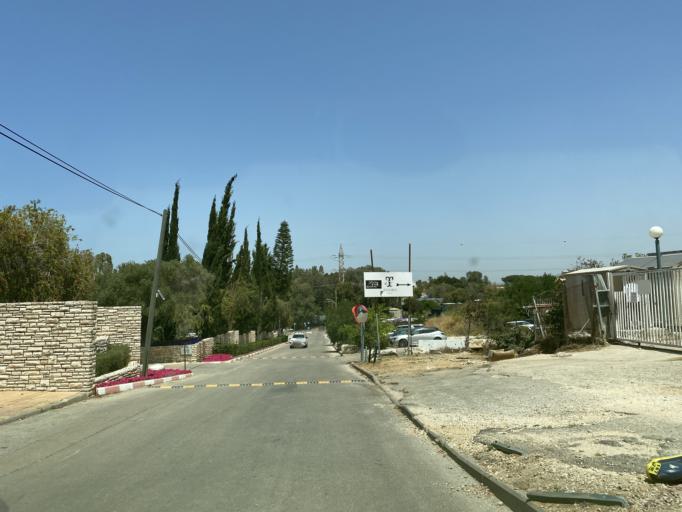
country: IL
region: Tel Aviv
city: Ramat HaSharon
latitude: 32.1301
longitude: 34.8276
